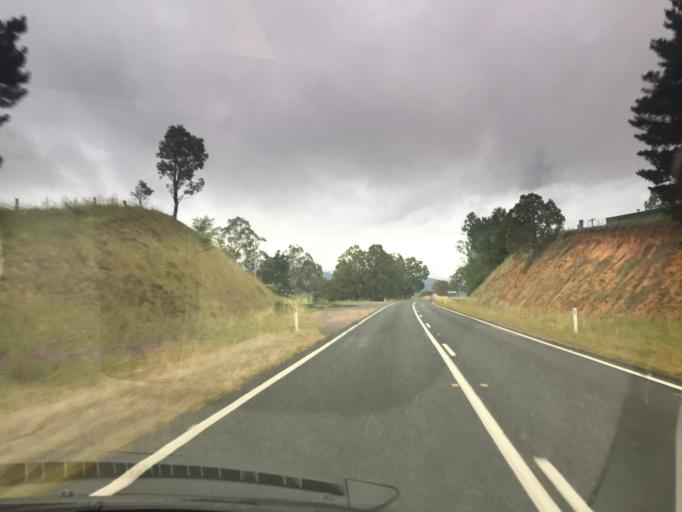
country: AU
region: New South Wales
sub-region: Bega Valley
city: Bega
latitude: -36.6136
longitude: 149.5419
